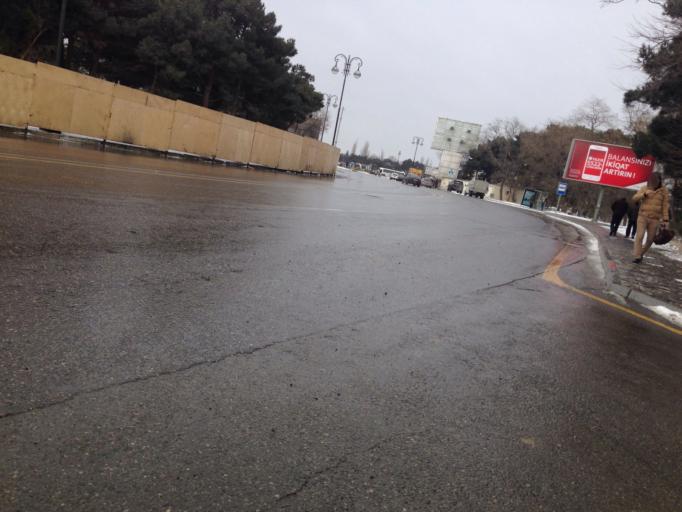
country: AZ
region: Baki
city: Baku
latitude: 40.3984
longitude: 49.8511
